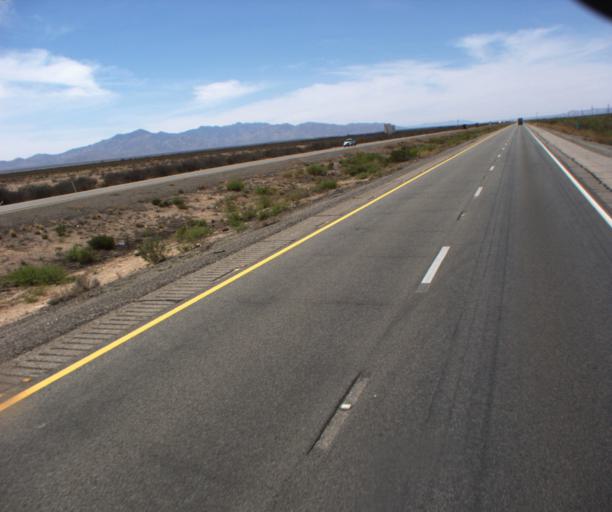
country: US
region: New Mexico
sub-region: Hidalgo County
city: Lordsburg
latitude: 32.2768
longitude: -109.2635
